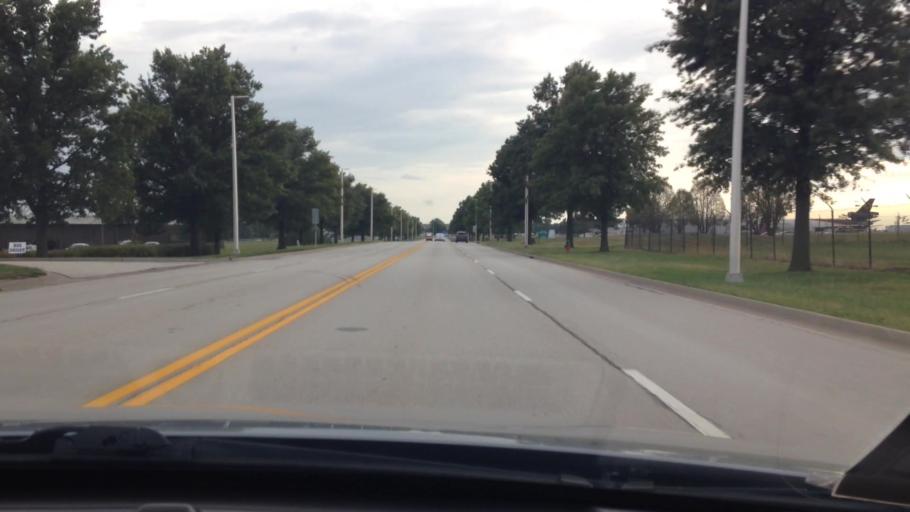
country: US
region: Missouri
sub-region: Platte County
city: Weatherby Lake
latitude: 39.3103
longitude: -94.7170
